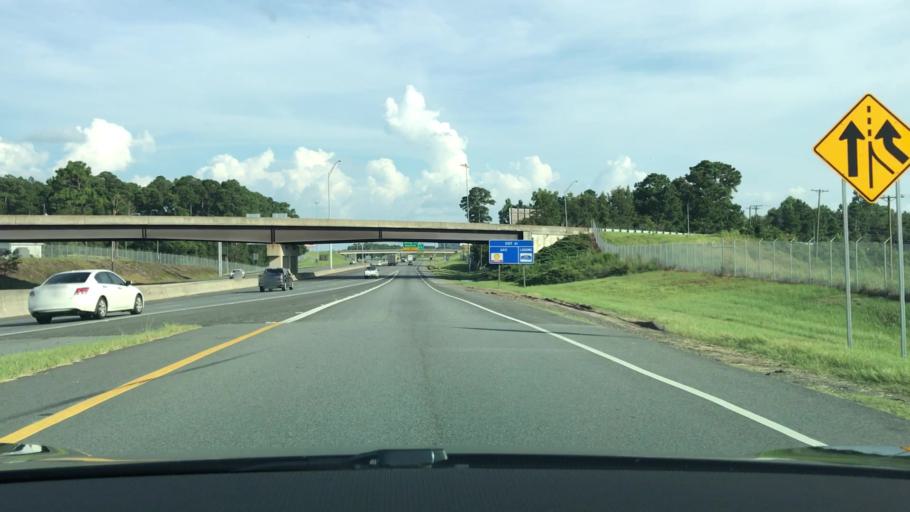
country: US
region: Georgia
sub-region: Tift County
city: Tifton
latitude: 31.4469
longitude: -83.5305
